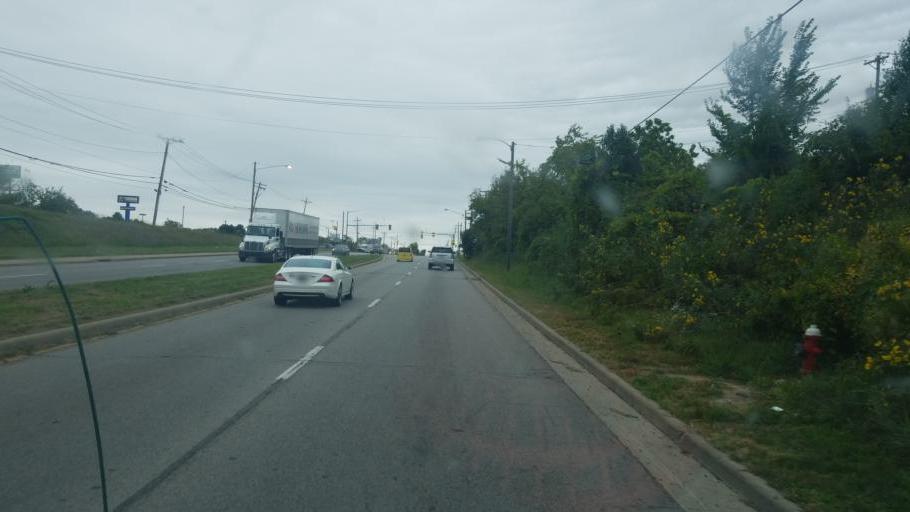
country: US
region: Ohio
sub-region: Lucas County
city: Ottawa Hills
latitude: 41.6250
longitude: -83.6644
